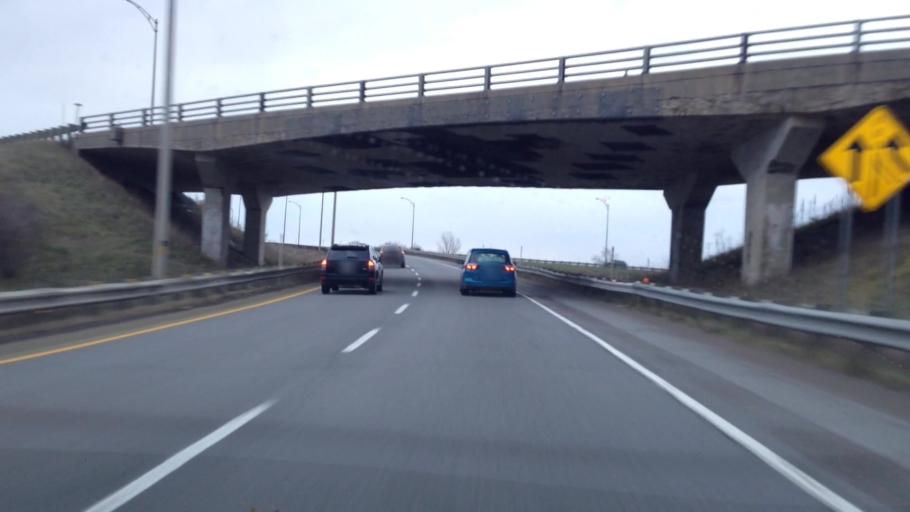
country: CA
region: Quebec
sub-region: Monteregie
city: Vaudreuil-Dorion
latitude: 45.3998
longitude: -74.0600
